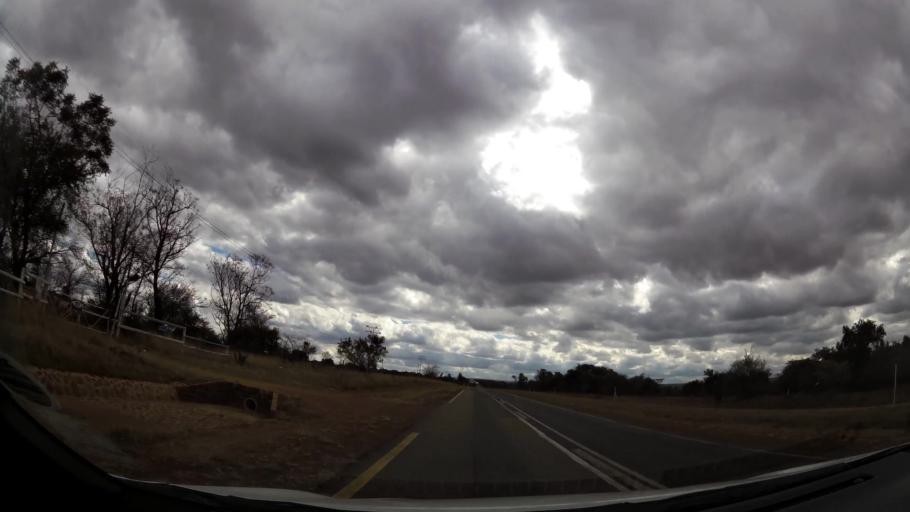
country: ZA
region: Limpopo
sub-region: Waterberg District Municipality
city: Modimolle
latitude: -24.7416
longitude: 28.4386
